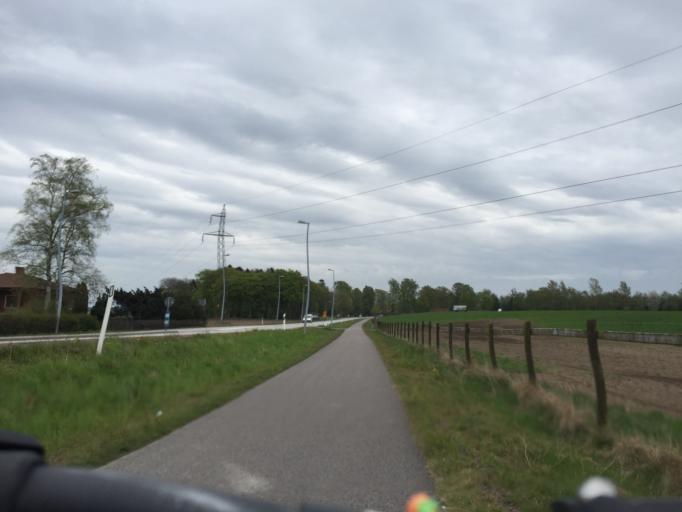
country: SE
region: Skane
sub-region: Lunds Kommun
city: Veberod
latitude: 55.6438
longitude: 13.4733
